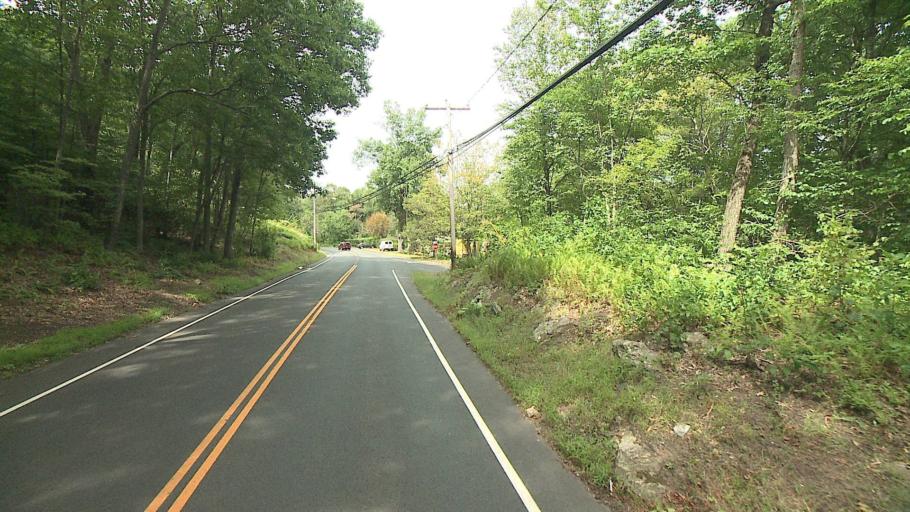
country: US
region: Connecticut
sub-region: Litchfield County
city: Plymouth
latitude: 41.6631
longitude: -73.0485
